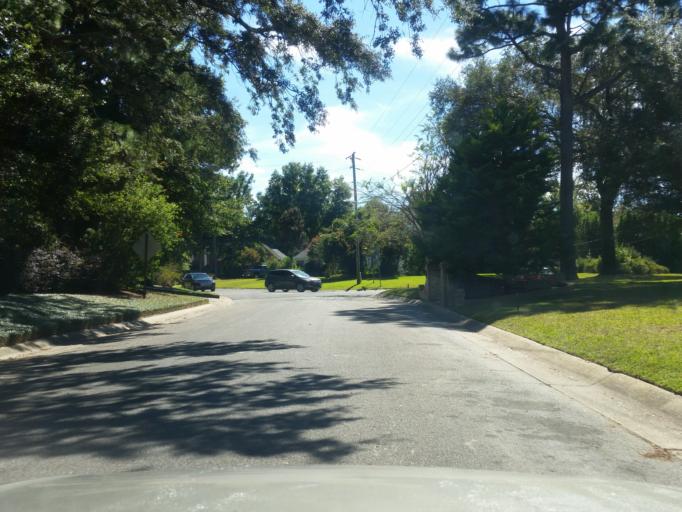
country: US
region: Florida
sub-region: Escambia County
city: East Pensacola Heights
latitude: 30.4734
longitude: -87.1693
